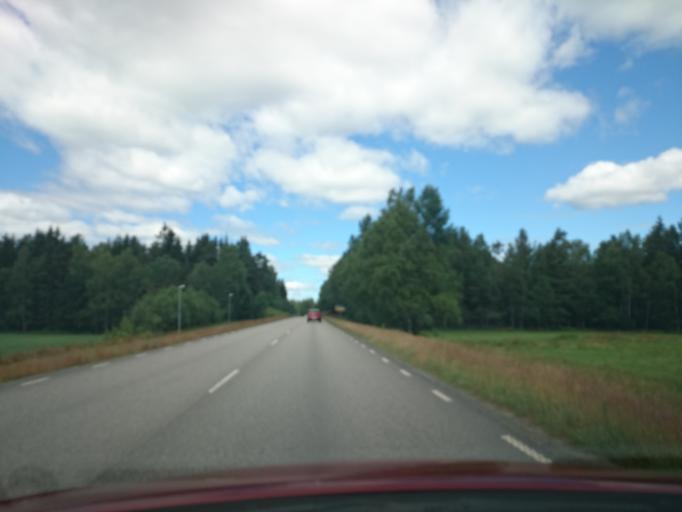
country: SE
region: Vaestra Goetaland
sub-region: Lerums Kommun
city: Grabo
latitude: 57.8211
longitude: 12.2978
